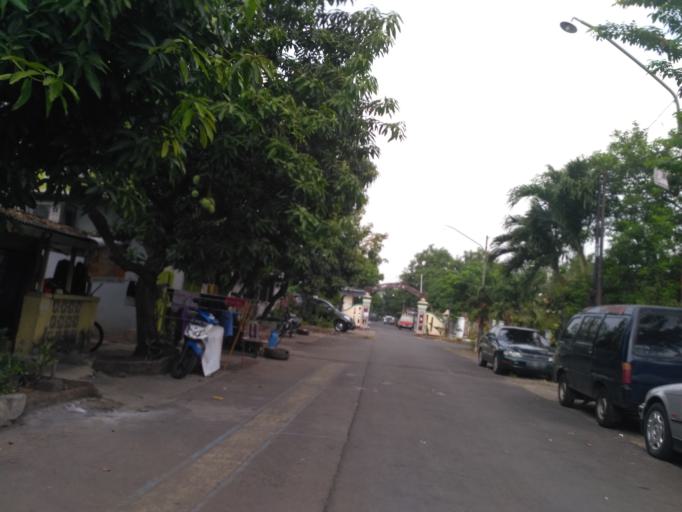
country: ID
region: Central Java
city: Semarang
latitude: -7.0079
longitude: 110.4411
